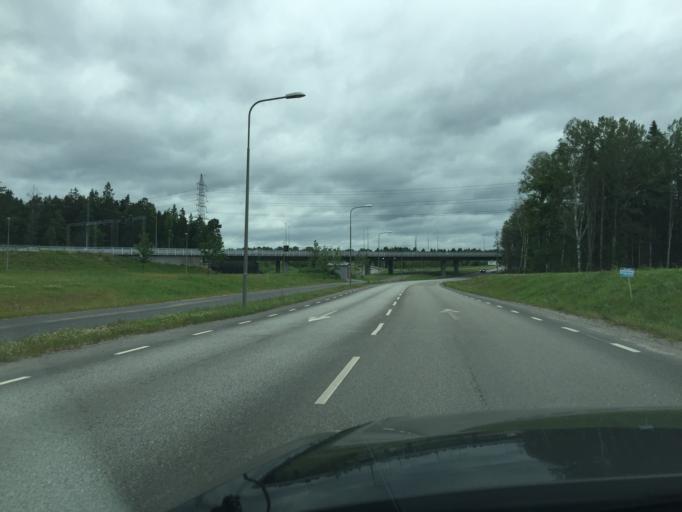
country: SE
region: Stockholm
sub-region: Stockholms Kommun
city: Kista
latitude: 59.4000
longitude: 17.9662
